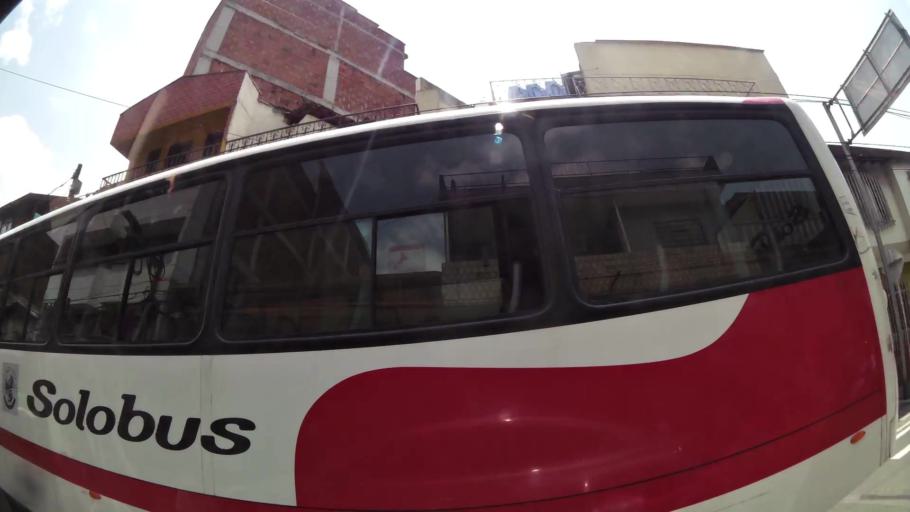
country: CO
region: Antioquia
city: Sabaneta
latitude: 6.1685
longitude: -75.6150
